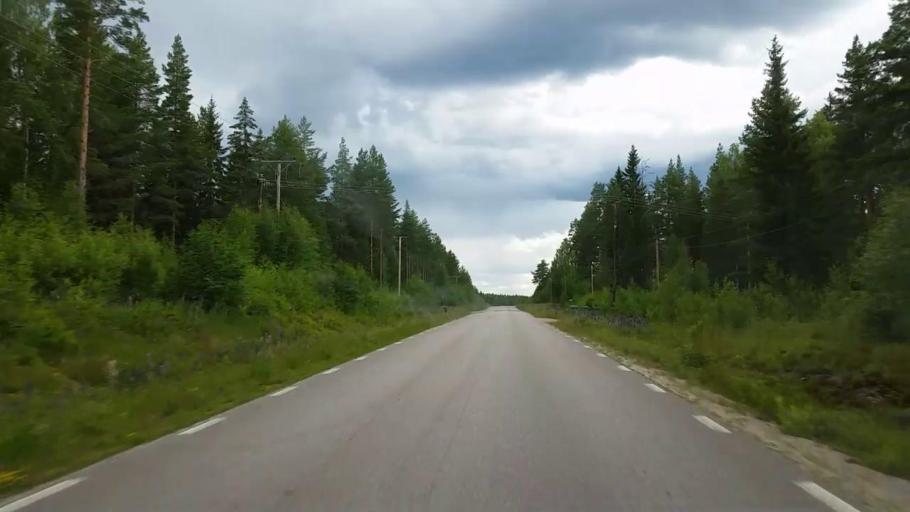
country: SE
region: Gaevleborg
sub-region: Ovanakers Kommun
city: Edsbyn
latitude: 61.4665
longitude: 15.8678
